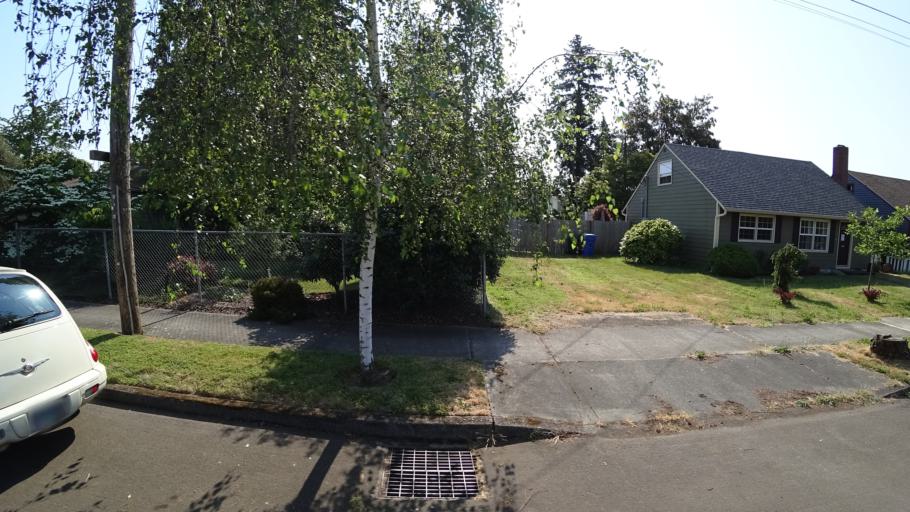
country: US
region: Oregon
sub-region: Multnomah County
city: Lents
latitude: 45.4623
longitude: -122.5987
